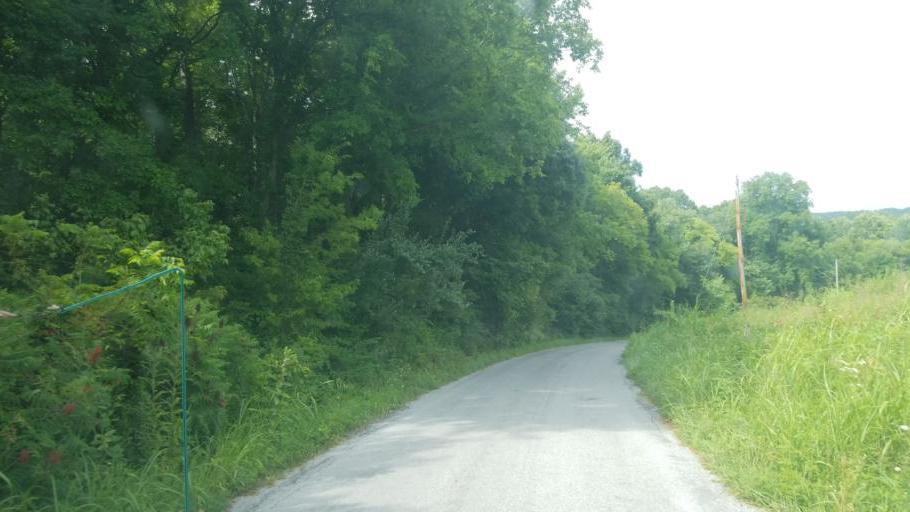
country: US
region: Illinois
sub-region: Union County
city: Cobden
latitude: 37.6144
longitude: -89.3424
